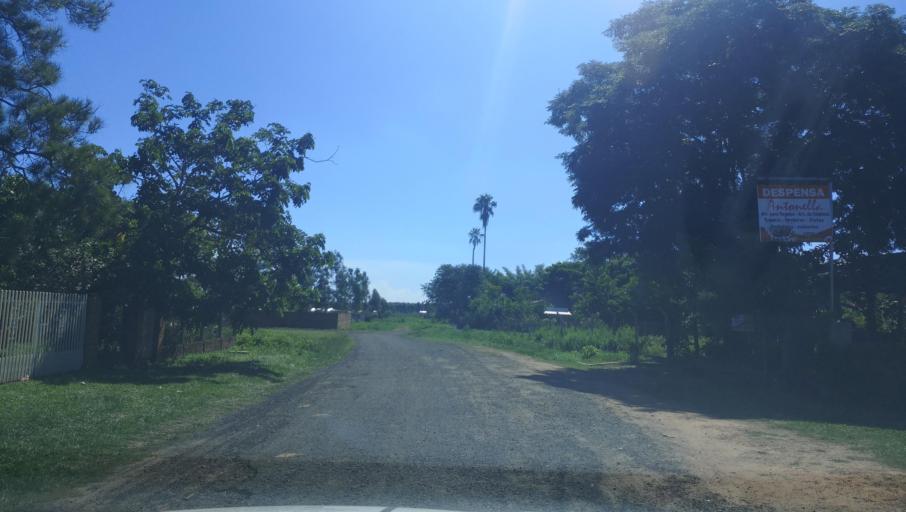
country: PY
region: Caaguazu
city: Carayao
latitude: -25.1940
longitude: -56.4047
